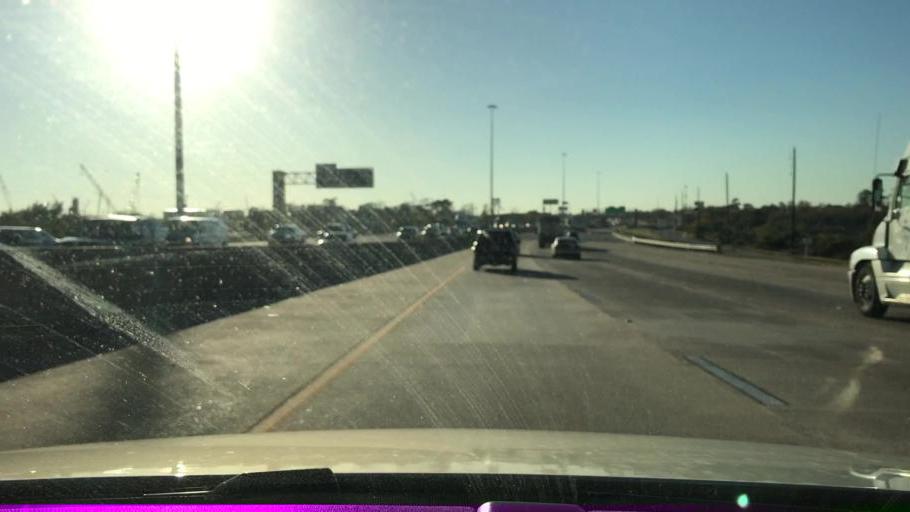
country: US
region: Texas
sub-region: Harris County
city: Channelview
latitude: 29.7919
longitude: -95.0816
